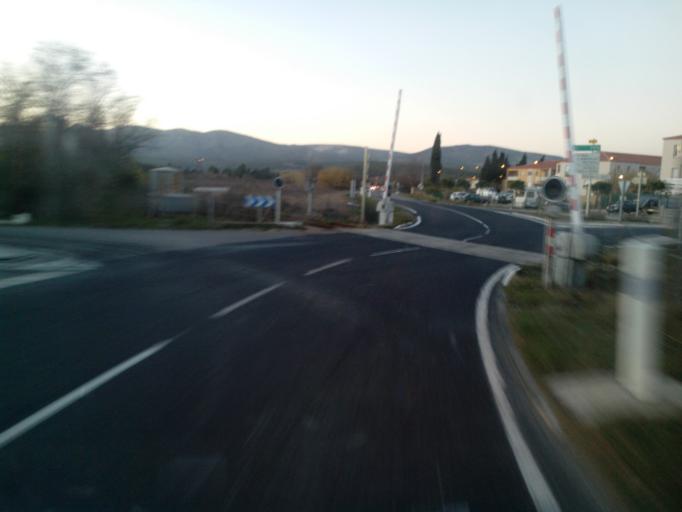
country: FR
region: Languedoc-Roussillon
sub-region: Departement des Pyrenees-Orientales
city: Peyrestortes
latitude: 42.7729
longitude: 2.8315
